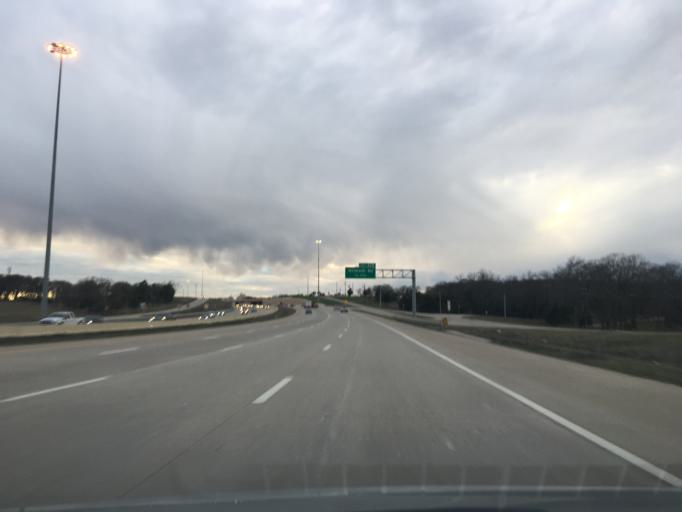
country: US
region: Texas
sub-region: Collin County
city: McKinney
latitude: 33.2453
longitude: -96.6253
